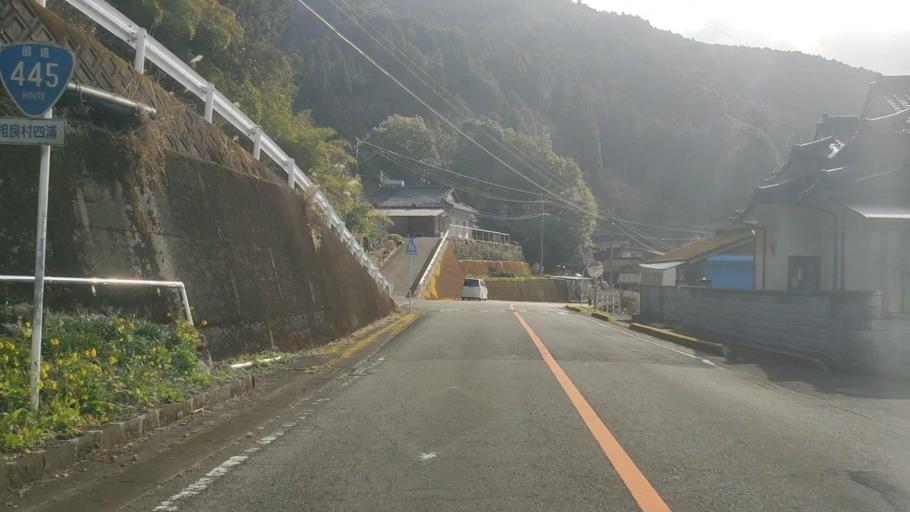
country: JP
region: Kumamoto
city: Hitoyoshi
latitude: 32.3146
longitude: 130.8465
